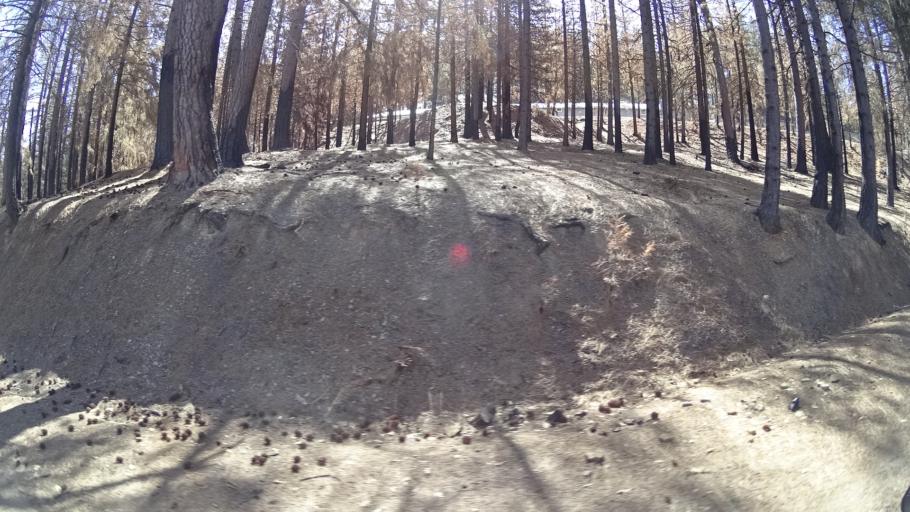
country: US
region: California
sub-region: Tehama County
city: Rancho Tehama Reserve
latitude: 39.6550
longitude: -122.7238
